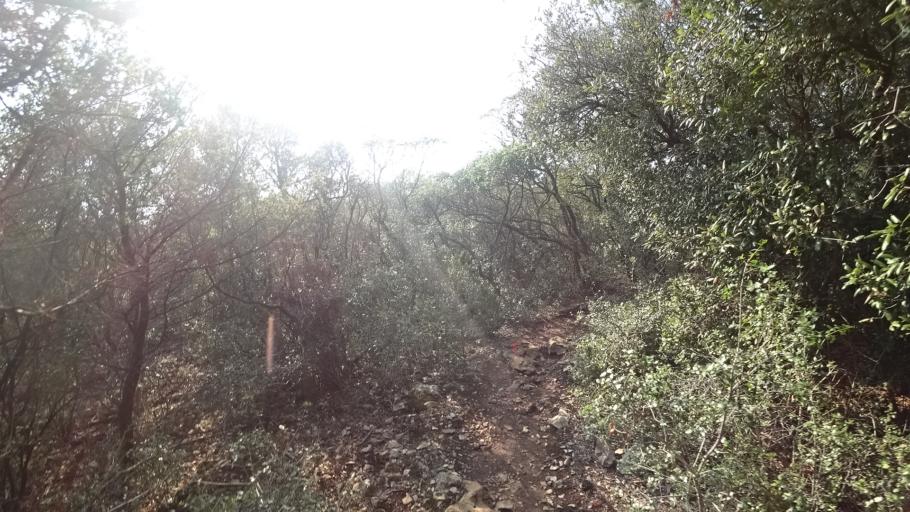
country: HR
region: Primorsko-Goranska
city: Mali Losinj
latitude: 44.4902
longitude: 14.5047
